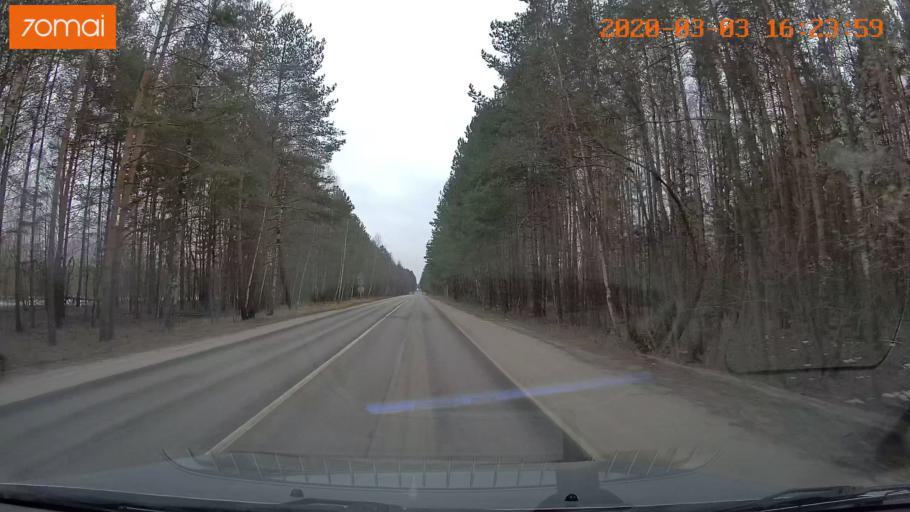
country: RU
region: Moskovskaya
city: Imeni Tsyurupy
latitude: 55.4744
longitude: 38.6572
